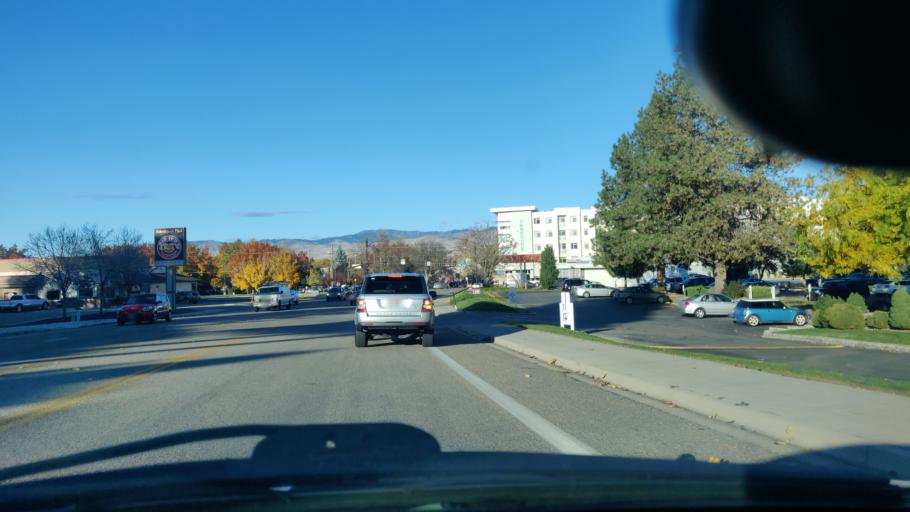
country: US
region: Idaho
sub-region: Ada County
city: Boise
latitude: 43.5968
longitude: -116.2058
